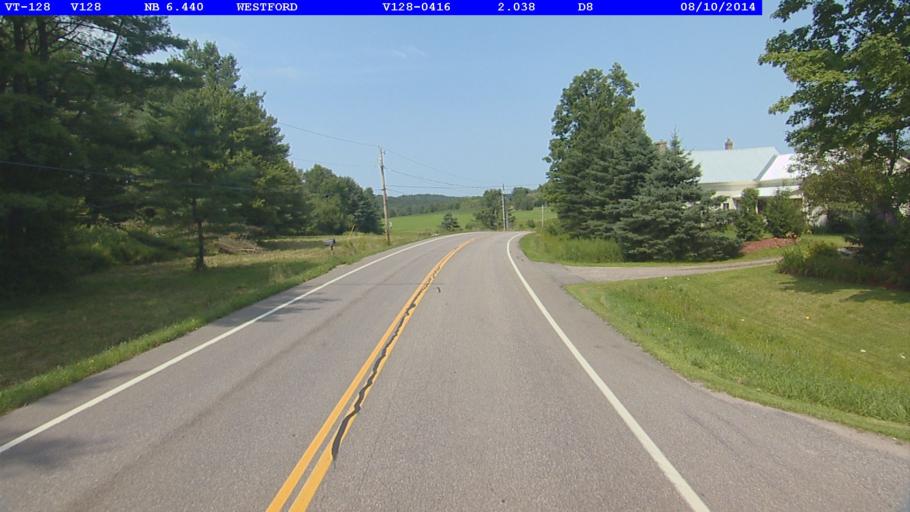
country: US
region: Vermont
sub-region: Chittenden County
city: Jericho
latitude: 44.5871
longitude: -73.0153
